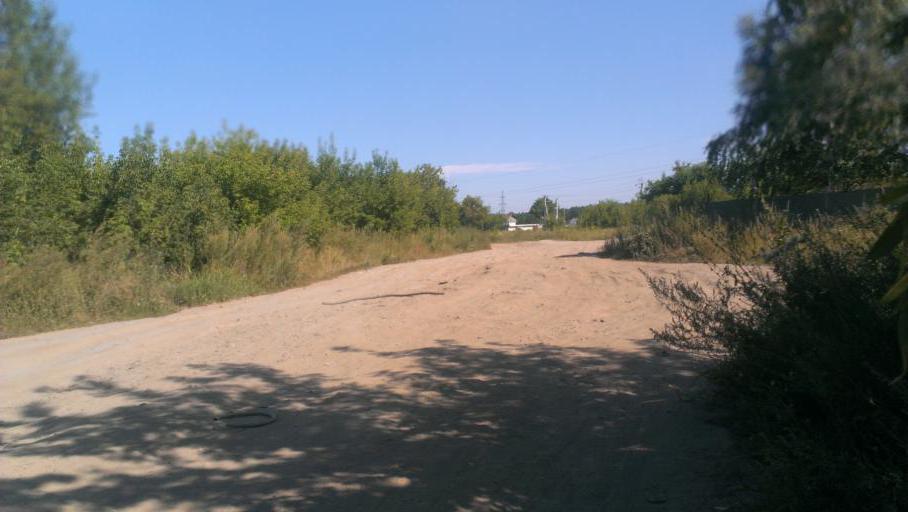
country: RU
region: Altai Krai
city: Novosilikatnyy
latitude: 53.3247
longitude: 83.6838
